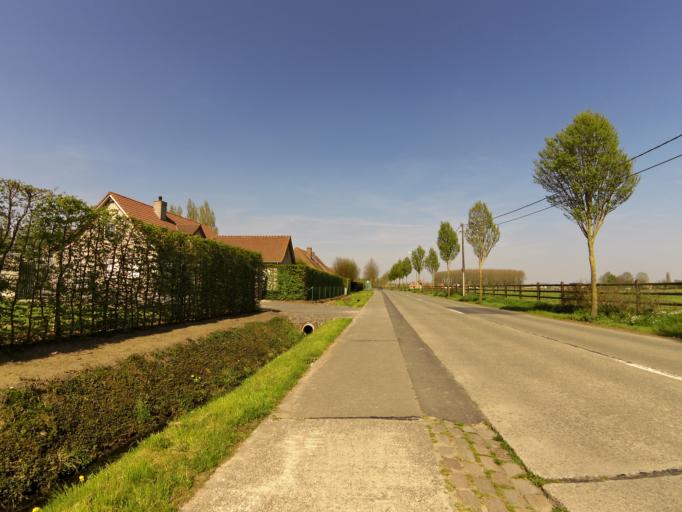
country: BE
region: Flanders
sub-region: Provincie West-Vlaanderen
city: Torhout
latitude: 51.0481
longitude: 3.0719
